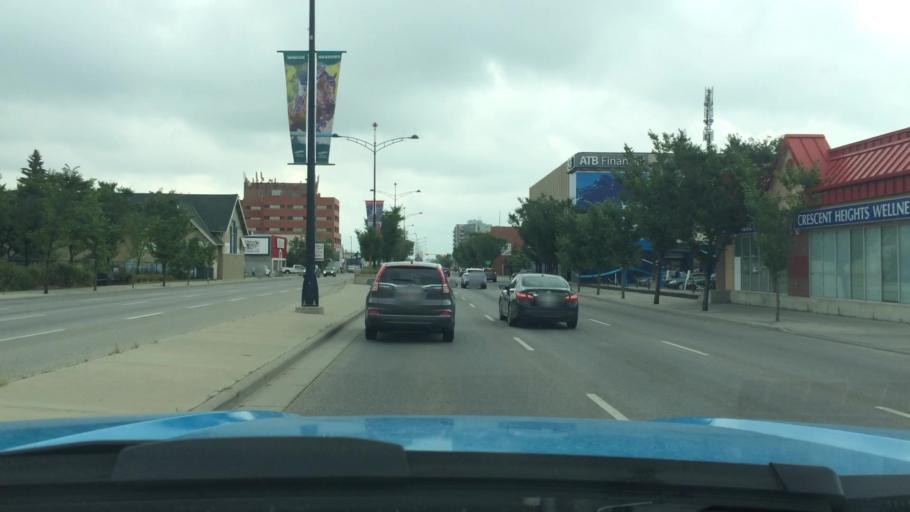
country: CA
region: Alberta
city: Calgary
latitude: 51.0669
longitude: -114.0667
